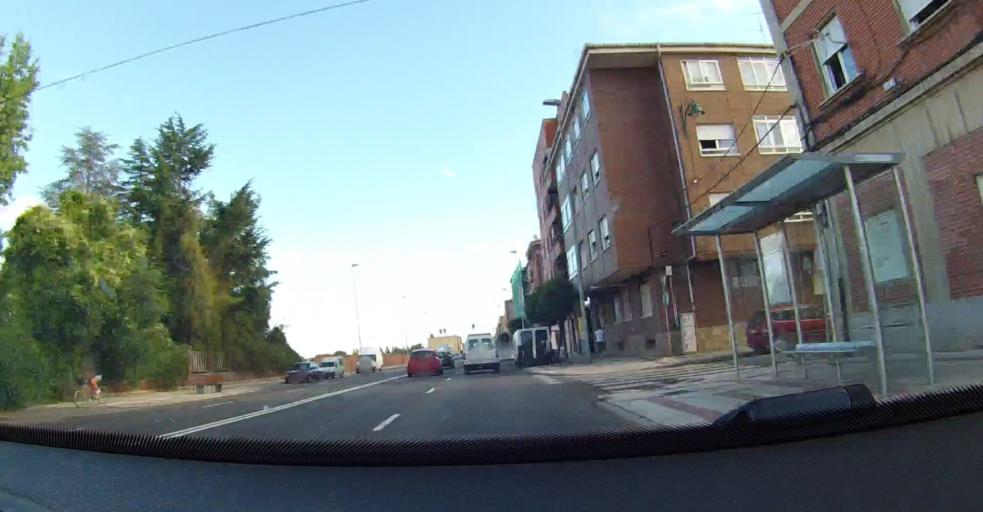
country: ES
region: Castille and Leon
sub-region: Provincia de Leon
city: Leon
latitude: 42.5905
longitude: -5.5848
